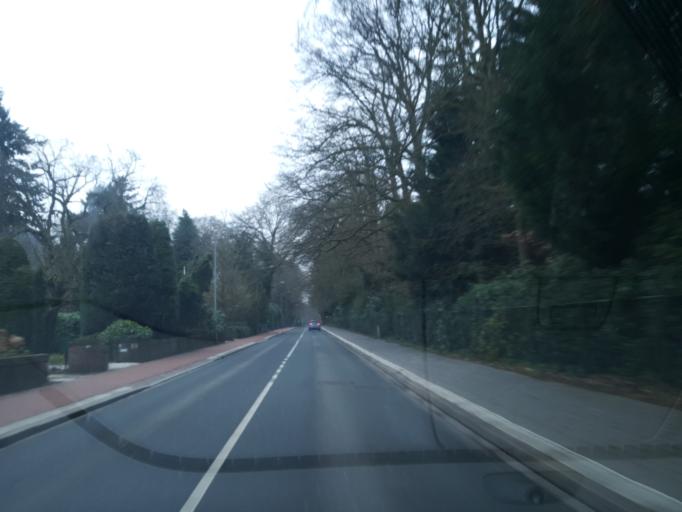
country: NL
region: North Holland
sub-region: Gemeente Hilversum
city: Hilversum
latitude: 52.2071
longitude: 5.1811
